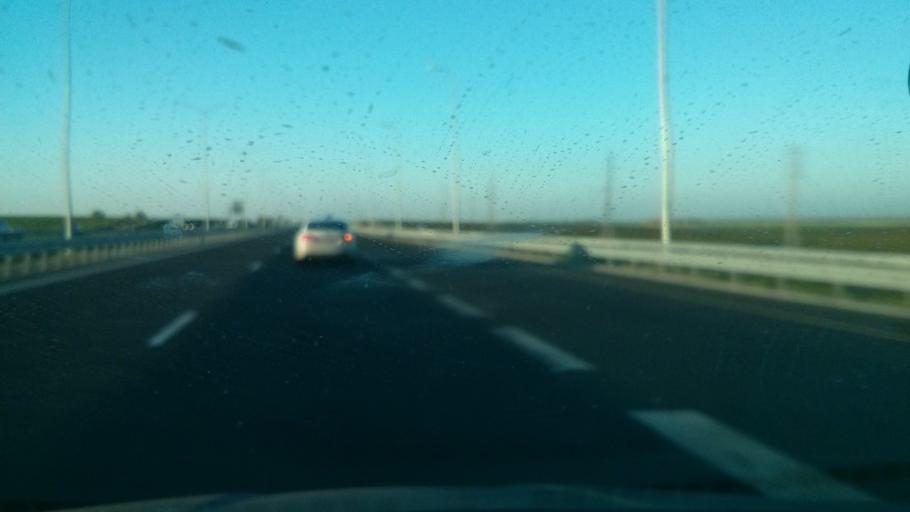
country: IL
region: Southern District
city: Lehavim
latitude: 31.4472
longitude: 34.7713
